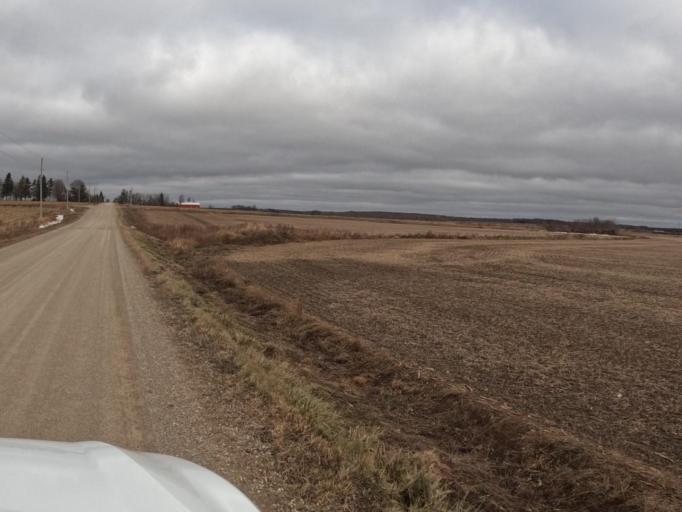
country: CA
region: Ontario
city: Shelburne
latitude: 44.0048
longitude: -80.4104
